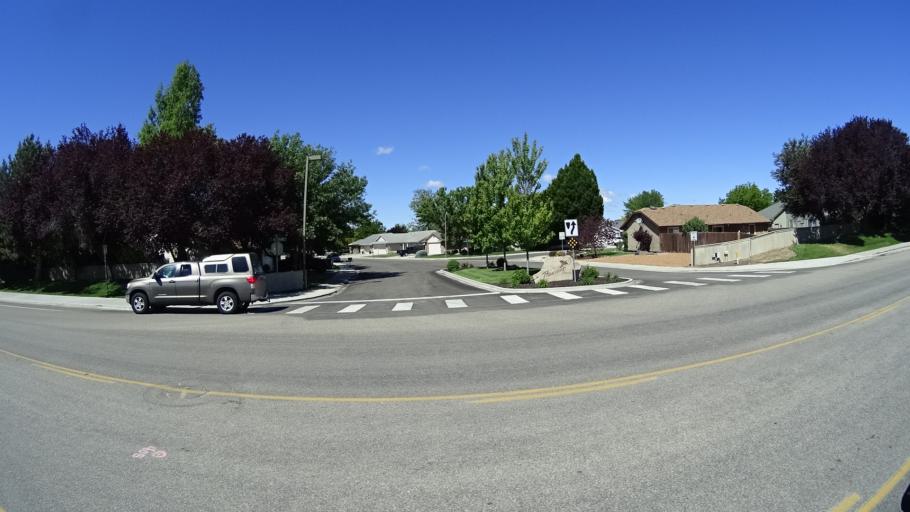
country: US
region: Idaho
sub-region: Ada County
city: Meridian
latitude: 43.6320
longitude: -116.3745
